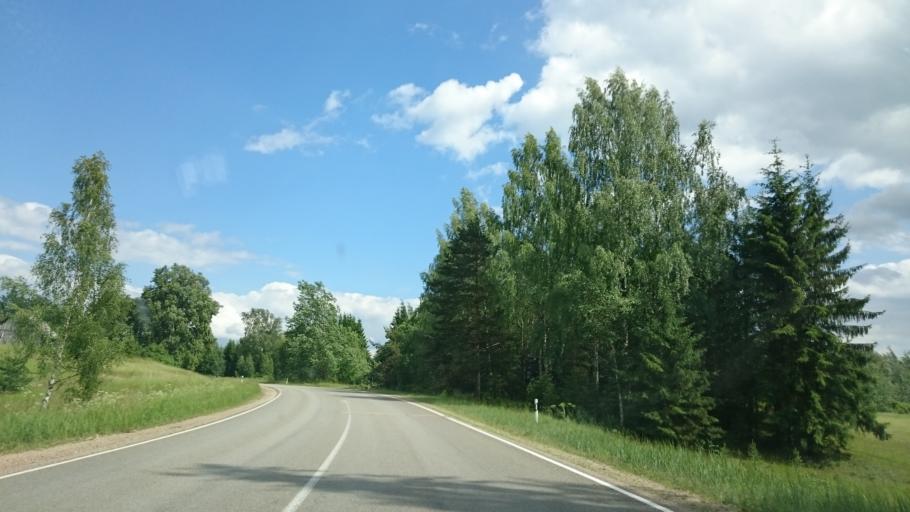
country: LV
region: Ludzas Rajons
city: Ludza
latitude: 56.5342
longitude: 27.5839
